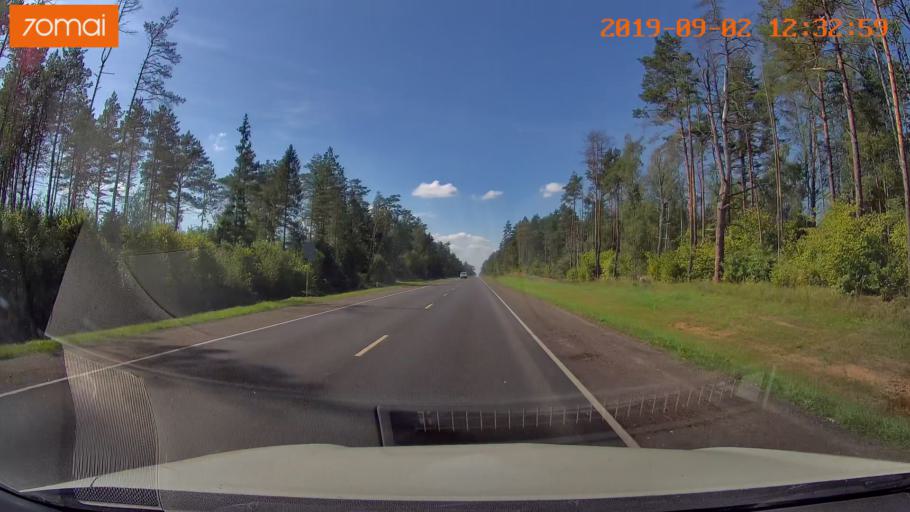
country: RU
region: Smolensk
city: Shumyachi
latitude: 53.8210
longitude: 32.4388
